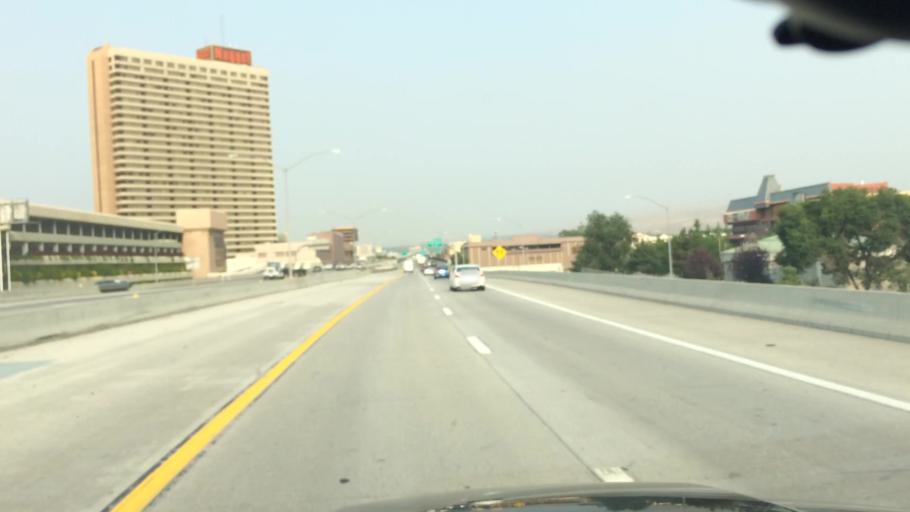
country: US
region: Nevada
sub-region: Washoe County
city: Sparks
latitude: 39.5340
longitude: -119.7539
